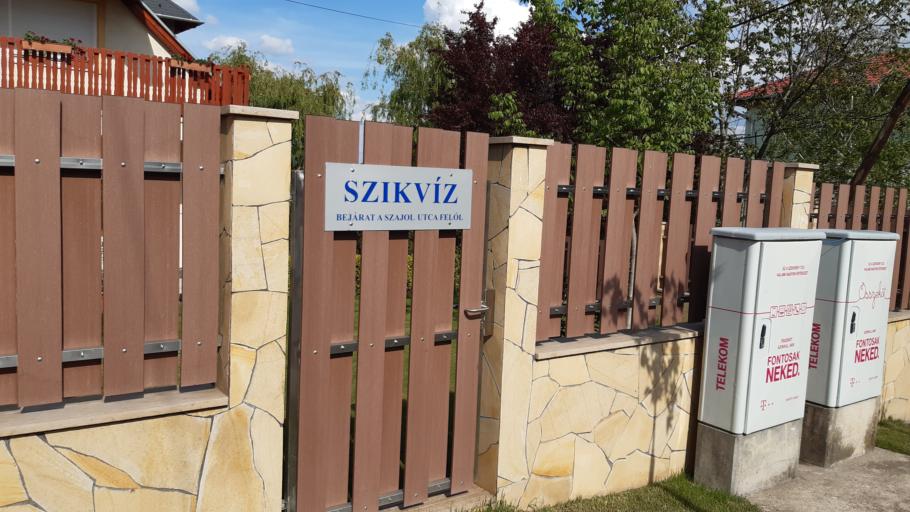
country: HU
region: Budapest
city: Budapest XXII. keruelet
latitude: 47.4447
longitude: 19.0231
